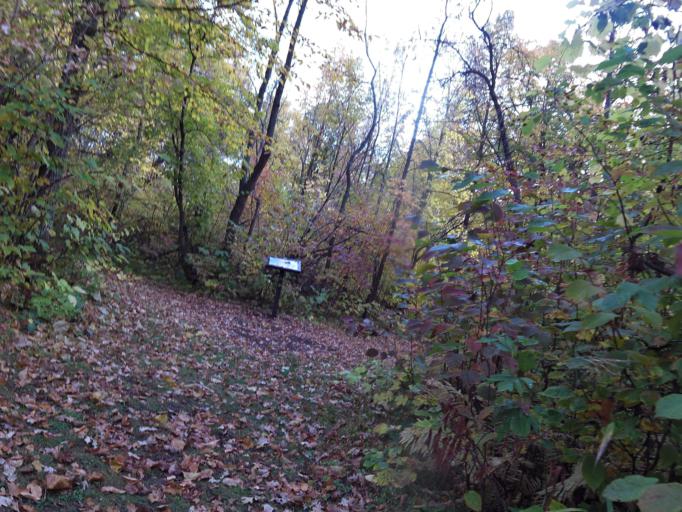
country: US
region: North Dakota
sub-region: Pembina County
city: Cavalier
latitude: 48.7779
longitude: -97.7368
